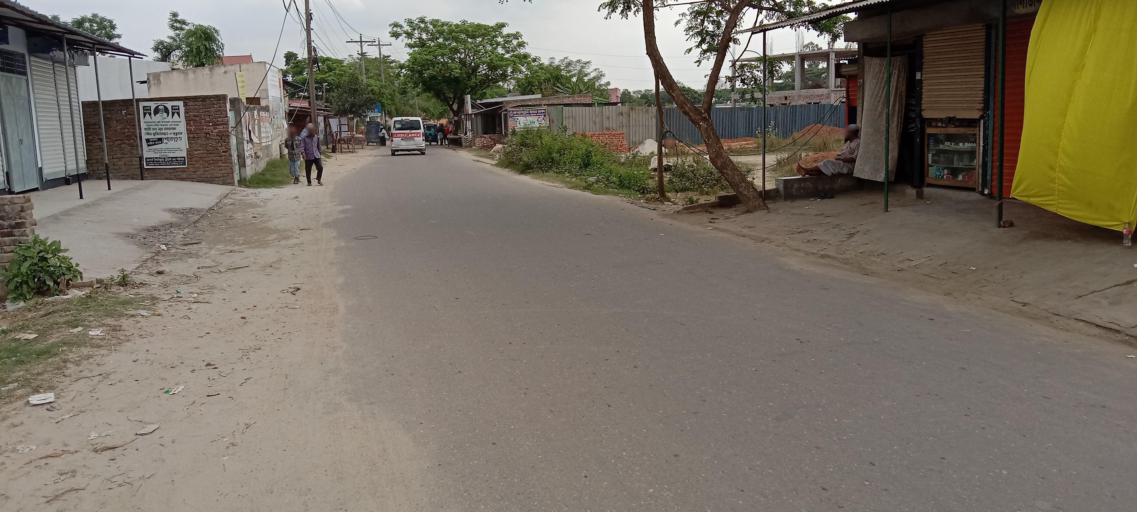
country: BD
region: Dhaka
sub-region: Dhaka
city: Dhaka
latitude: 23.6569
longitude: 90.4154
